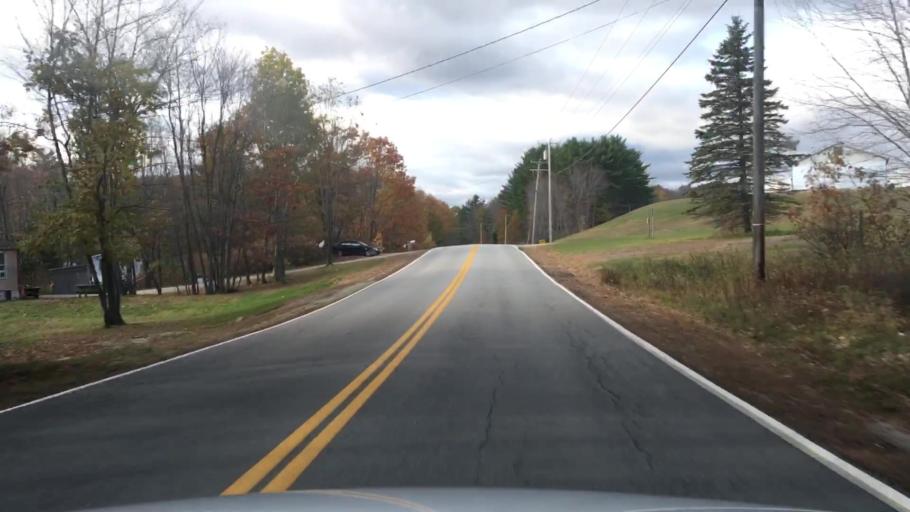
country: US
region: Maine
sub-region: Androscoggin County
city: Leeds
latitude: 44.3280
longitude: -70.1225
